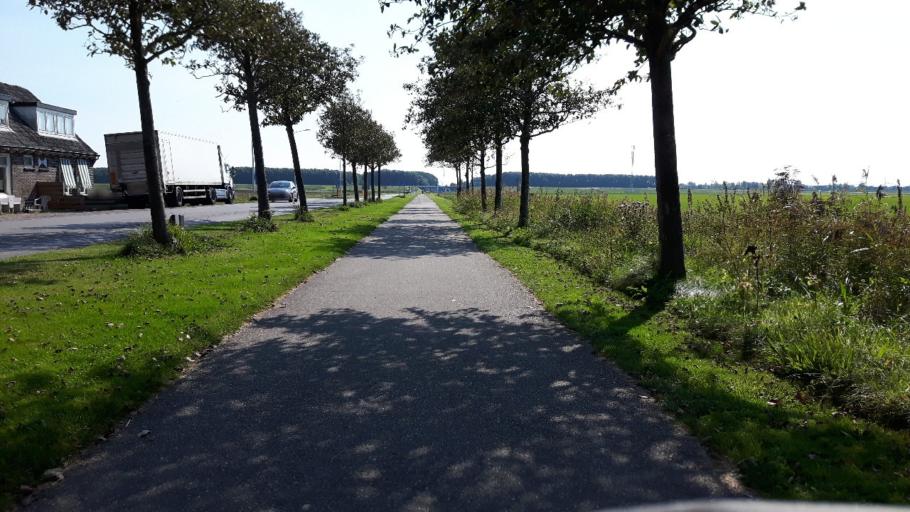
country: NL
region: Friesland
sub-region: Gemeente Franekeradeel
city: Franeker
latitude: 53.2071
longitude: 5.5421
